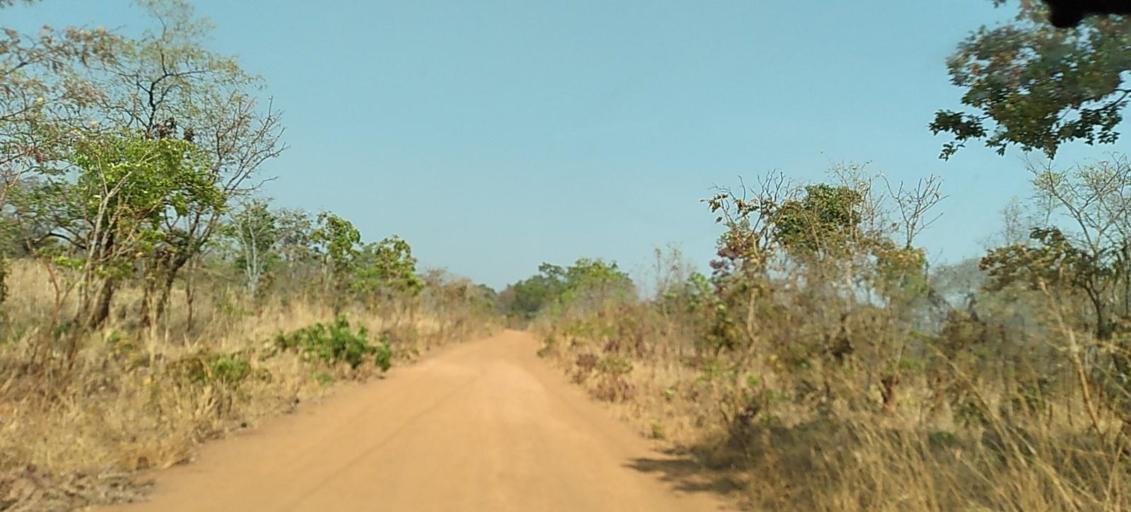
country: ZM
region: North-Western
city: Kasempa
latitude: -13.3897
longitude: 25.6821
